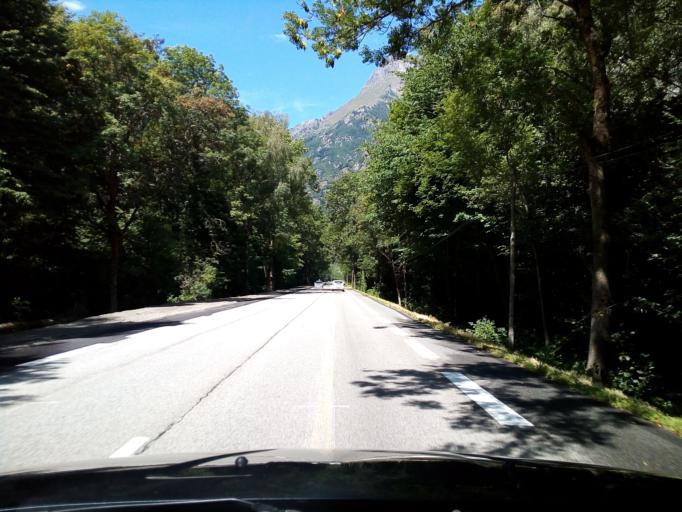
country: FR
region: Rhone-Alpes
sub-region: Departement de l'Isere
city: Livet-et-Gavet
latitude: 45.1171
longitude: 5.9824
